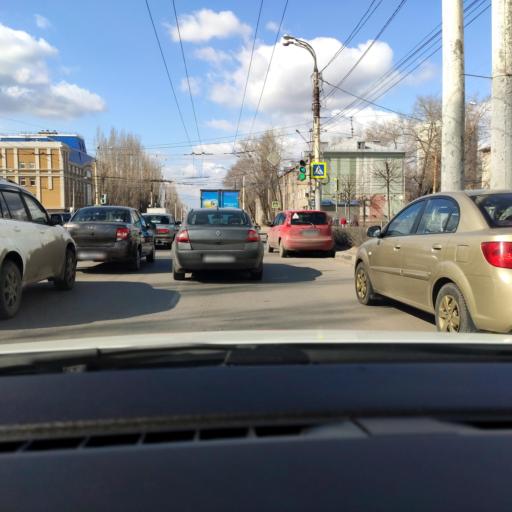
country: RU
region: Voronezj
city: Shilovo
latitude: 51.4401
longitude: 39.0907
